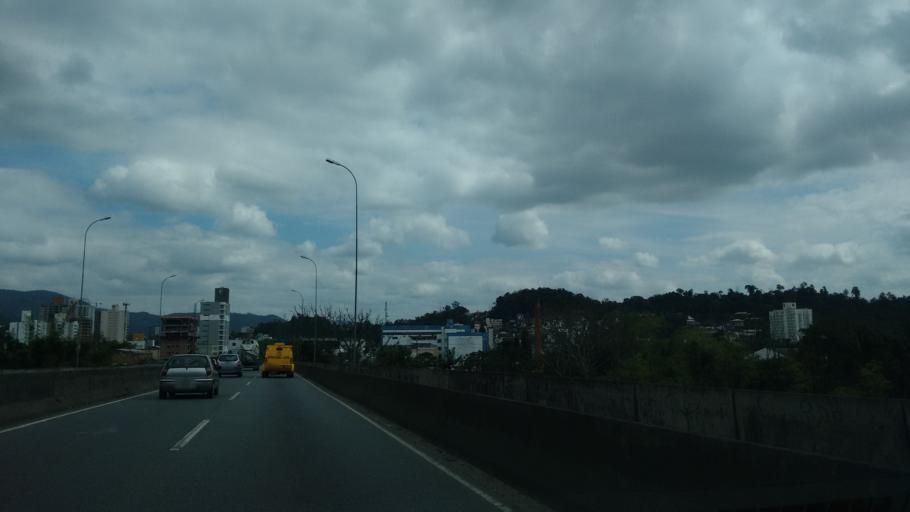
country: BR
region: Santa Catarina
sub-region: Blumenau
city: Blumenau
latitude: -26.8973
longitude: -49.0756
